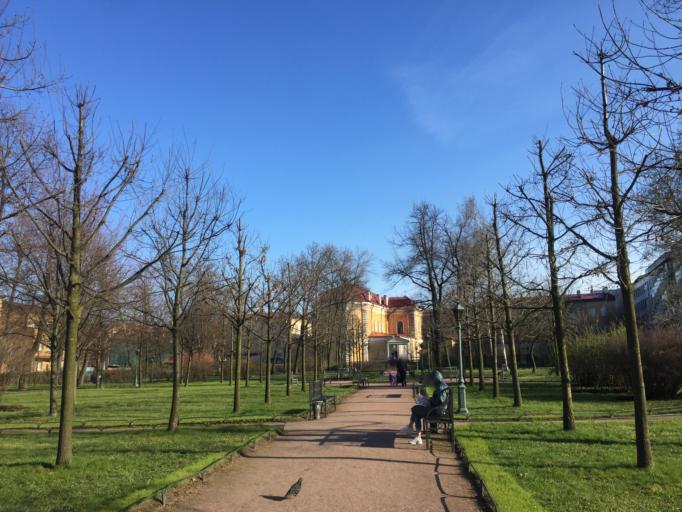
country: RU
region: St.-Petersburg
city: Saint Petersburg
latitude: 59.9180
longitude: 30.3113
